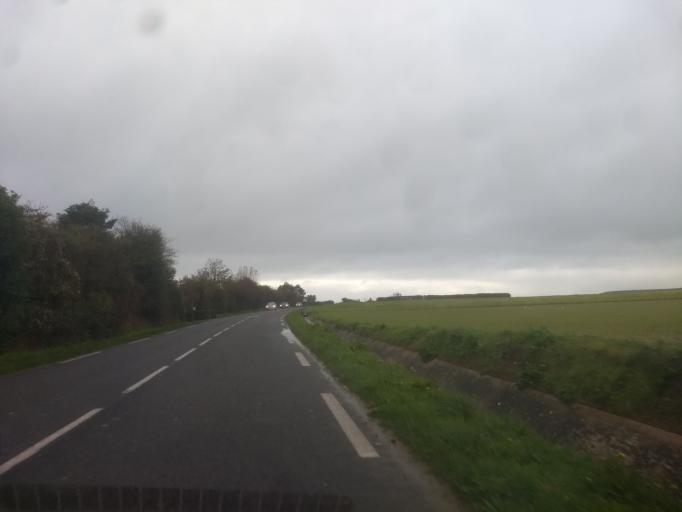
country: FR
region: Nord-Pas-de-Calais
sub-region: Departement du Pas-de-Calais
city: Wissant
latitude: 50.8992
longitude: 1.6838
